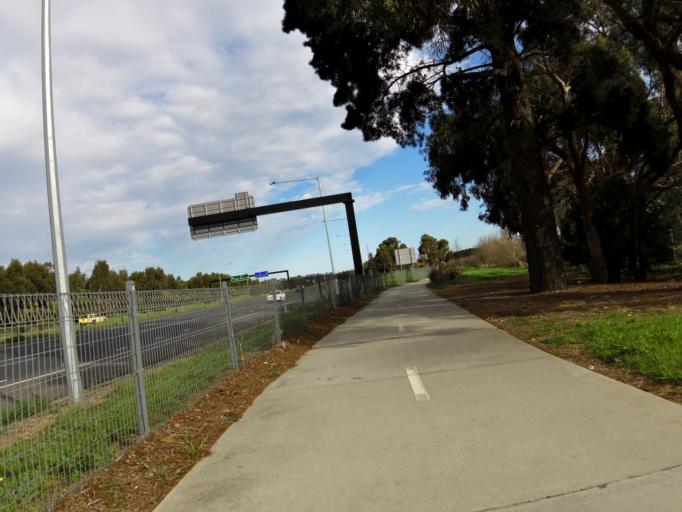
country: AU
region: Victoria
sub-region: Knox
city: Wantirna South
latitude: -37.8703
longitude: 145.2111
